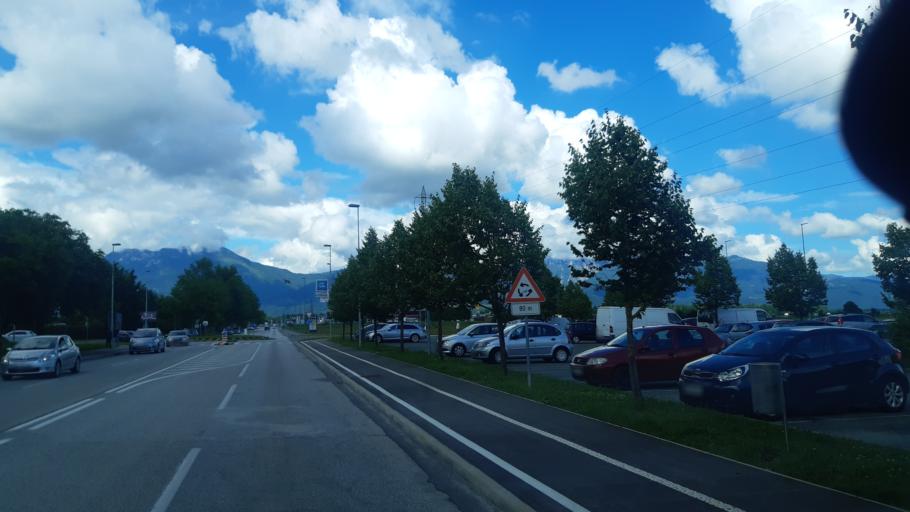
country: SI
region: Kranj
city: Kranj
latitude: 46.2377
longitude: 14.3698
